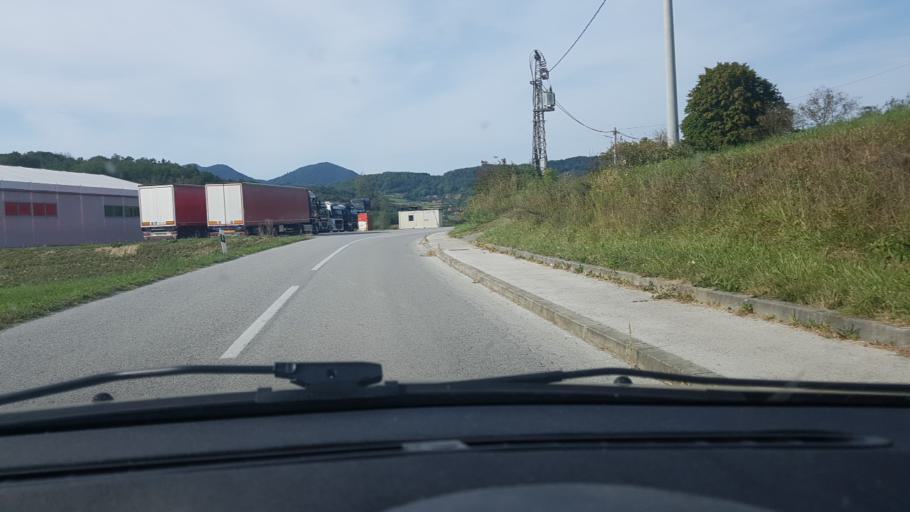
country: HR
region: Krapinsko-Zagorska
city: Mihovljan
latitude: 46.1402
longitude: 15.9640
